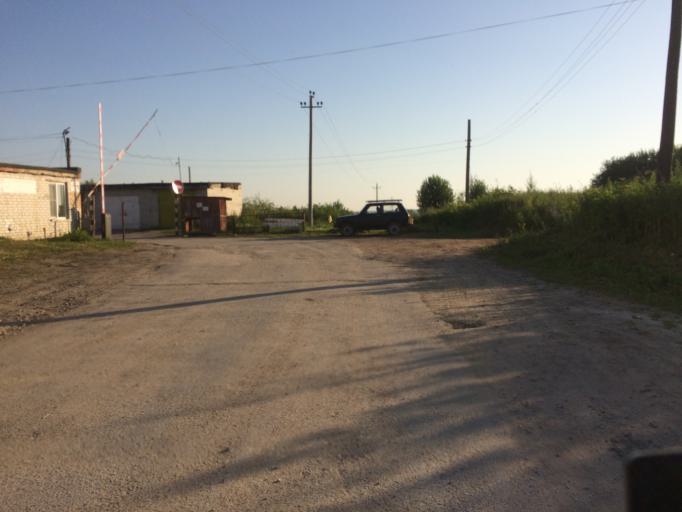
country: RU
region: Mariy-El
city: Yoshkar-Ola
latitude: 56.6566
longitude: 47.8881
